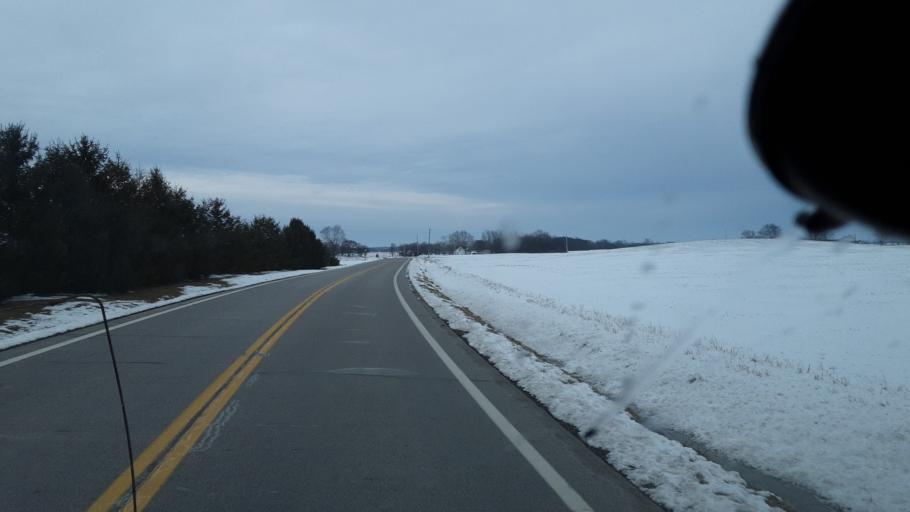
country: US
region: Ohio
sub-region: Pickaway County
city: Circleville
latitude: 39.6249
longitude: -83.0285
